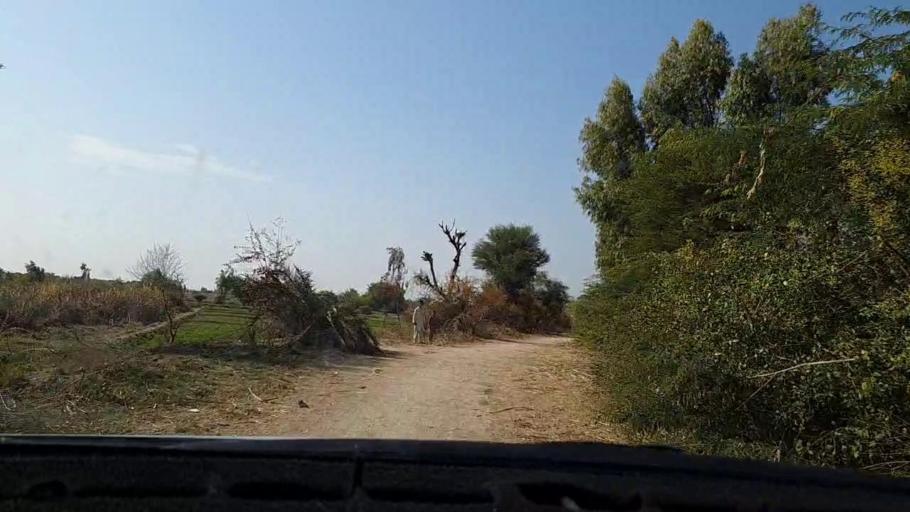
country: PK
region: Sindh
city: Tando Mittha Khan
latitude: 25.8112
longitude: 69.2945
